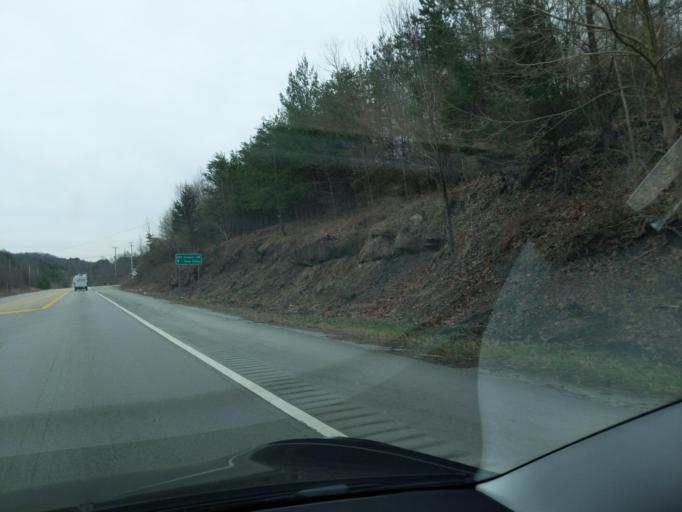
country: US
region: Kentucky
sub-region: Whitley County
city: Corbin
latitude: 36.9168
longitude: -84.0907
